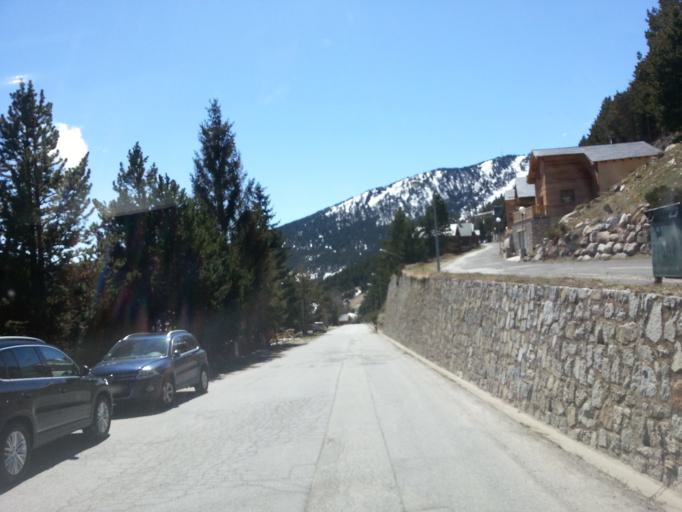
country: ES
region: Catalonia
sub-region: Provincia de Girona
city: Llivia
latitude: 42.5851
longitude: 2.0744
